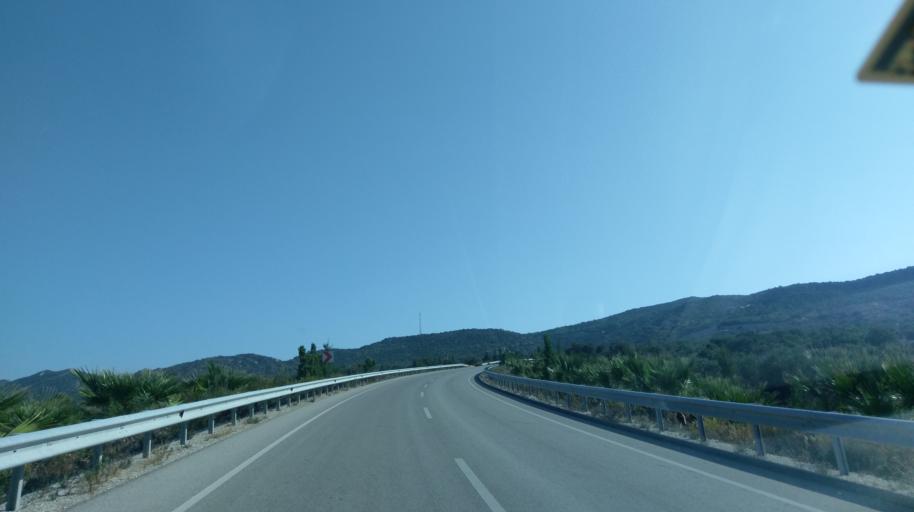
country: CY
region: Ammochostos
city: Trikomo
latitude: 35.4377
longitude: 33.9582
